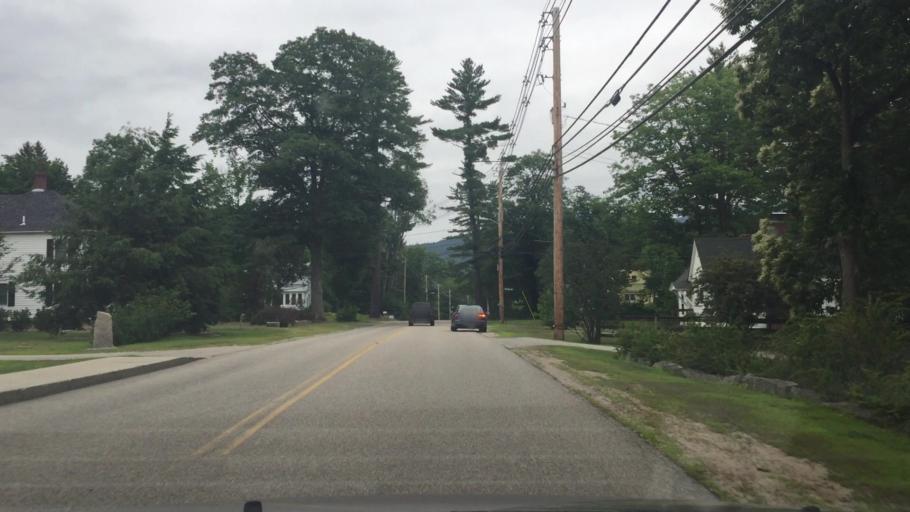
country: US
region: New Hampshire
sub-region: Carroll County
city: North Conway
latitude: 44.0546
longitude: -71.1190
